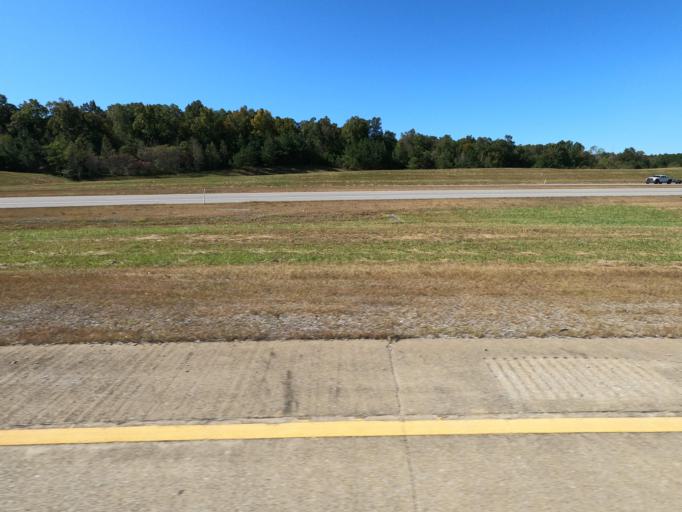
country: US
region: Tennessee
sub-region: Williamson County
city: Fairview
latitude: 35.9355
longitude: -87.1862
